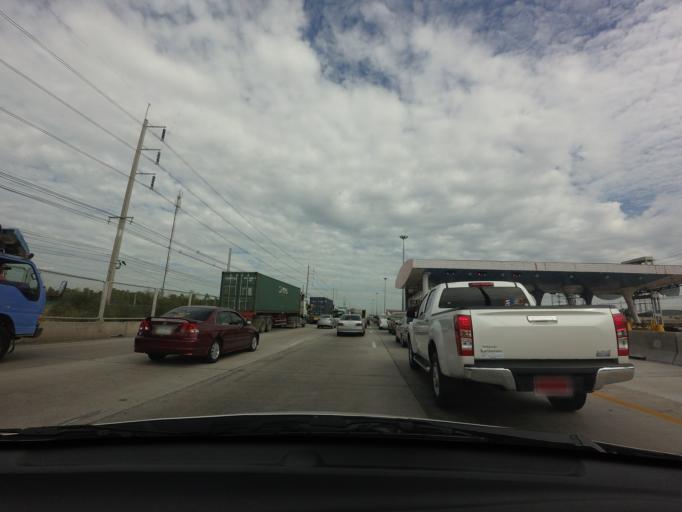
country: TH
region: Pathum Thani
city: Lam Luk Ka
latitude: 13.9715
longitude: 100.7128
